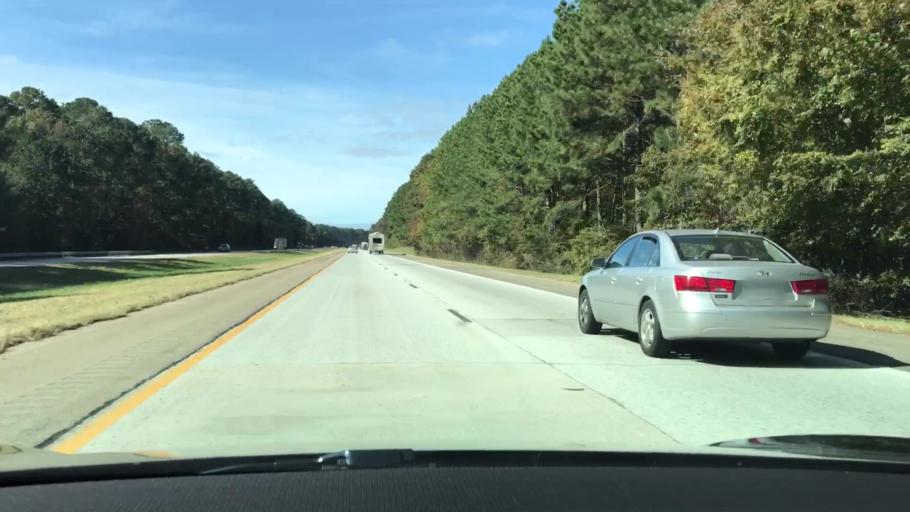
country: US
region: Georgia
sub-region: Putnam County
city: Jefferson
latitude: 33.5337
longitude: -83.2794
